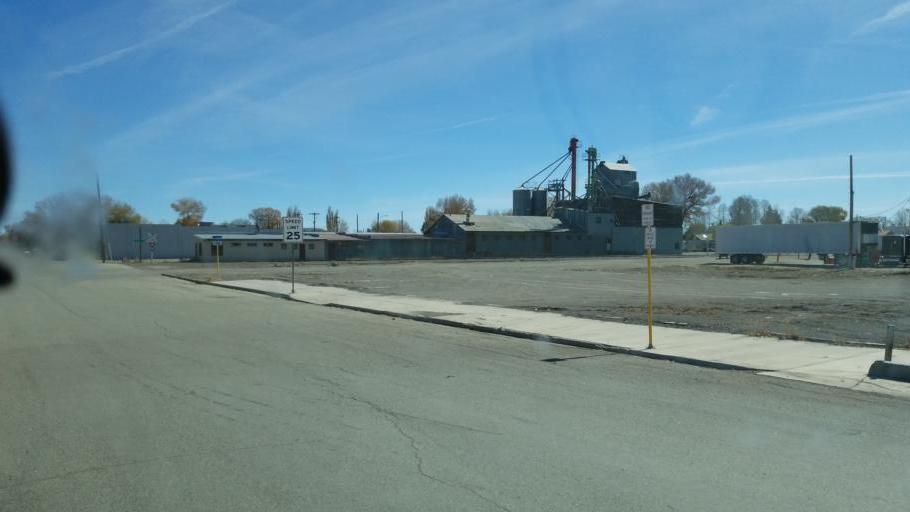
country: US
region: Colorado
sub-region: Conejos County
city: Conejos
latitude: 37.2752
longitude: -105.9617
